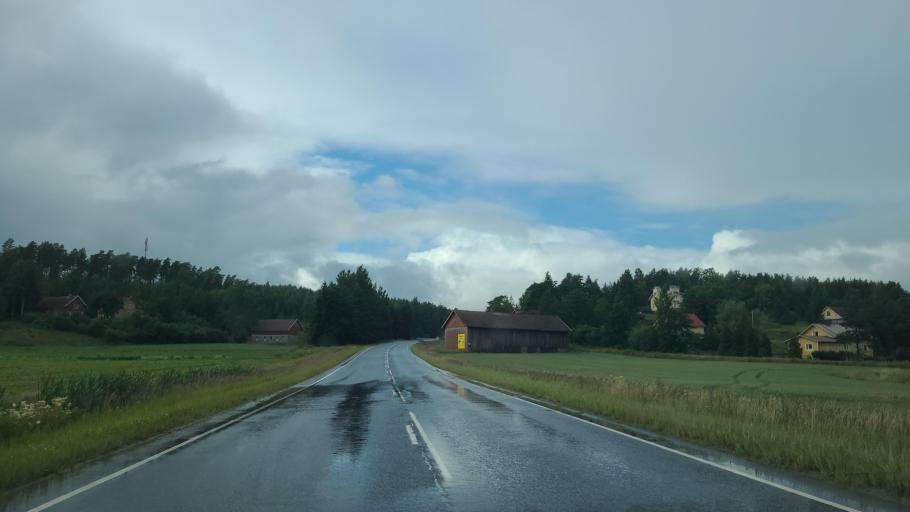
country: FI
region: Varsinais-Suomi
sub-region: Turku
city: Sauvo
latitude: 60.3331
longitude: 22.7089
